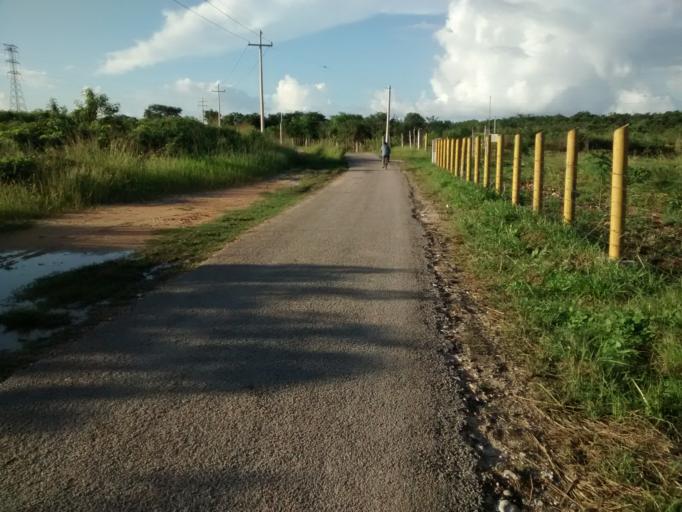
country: MX
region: Yucatan
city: Valladolid
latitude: 20.7076
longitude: -88.2152
